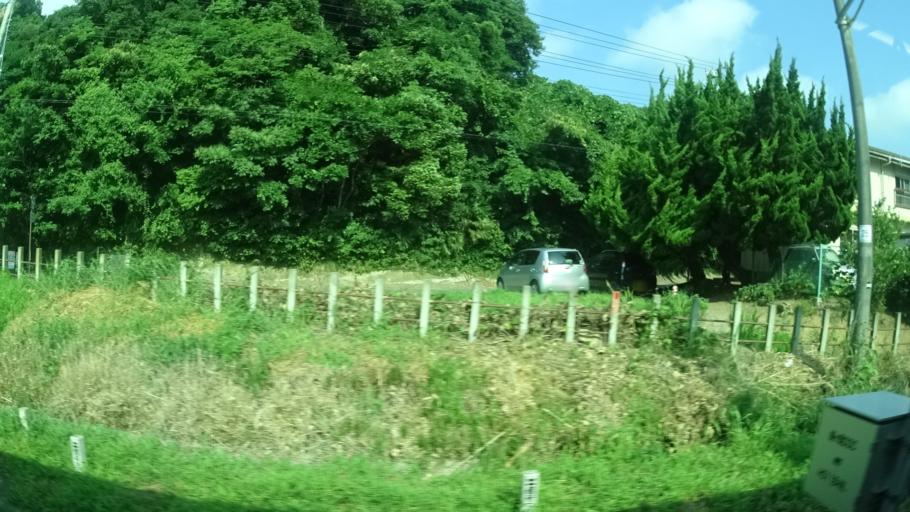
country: JP
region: Fukushima
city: Iwaki
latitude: 37.1062
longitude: 140.9836
